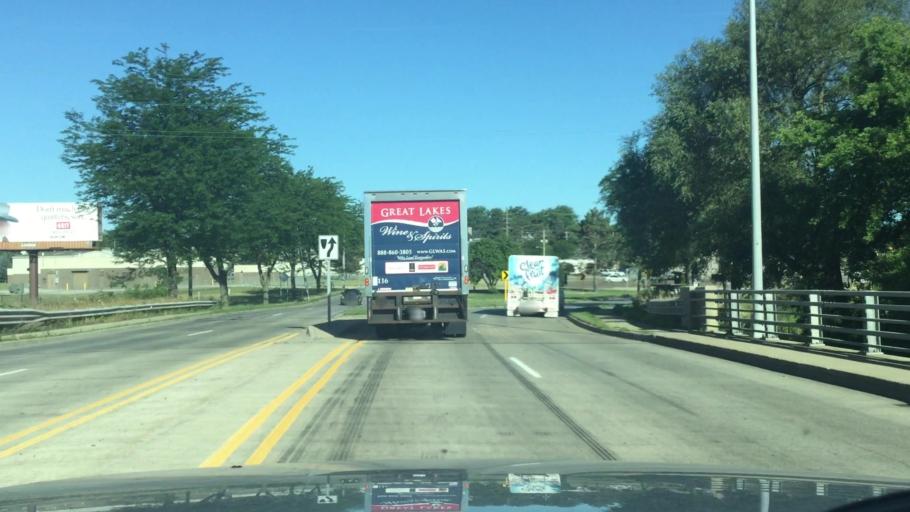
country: US
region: Michigan
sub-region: Saginaw County
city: Saginaw
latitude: 43.4108
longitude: -83.9663
